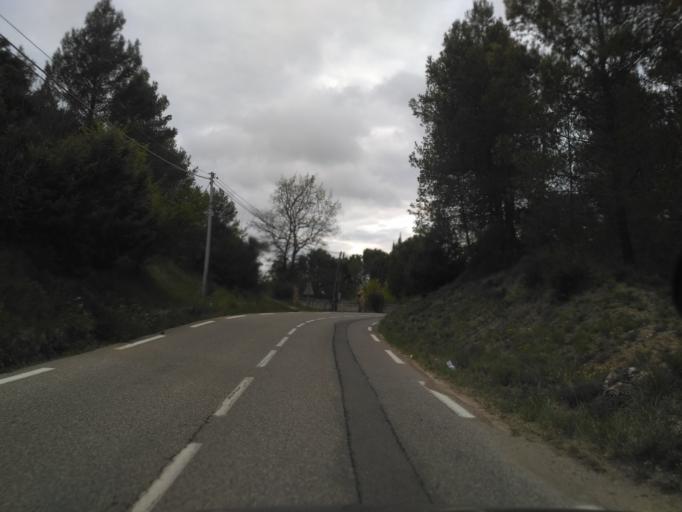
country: FR
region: Provence-Alpes-Cote d'Azur
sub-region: Departement du Var
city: Barjols
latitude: 43.6028
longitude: 5.9549
